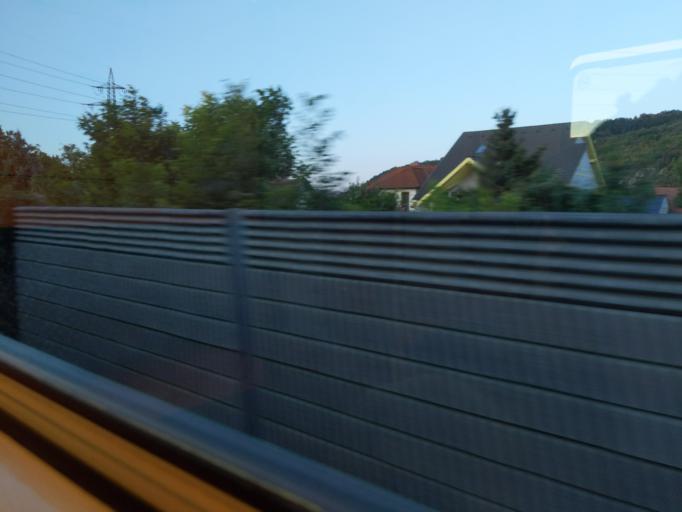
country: AT
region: Lower Austria
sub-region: Politischer Bezirk Korneuburg
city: Langenzersdorf
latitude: 48.3139
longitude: 16.3490
